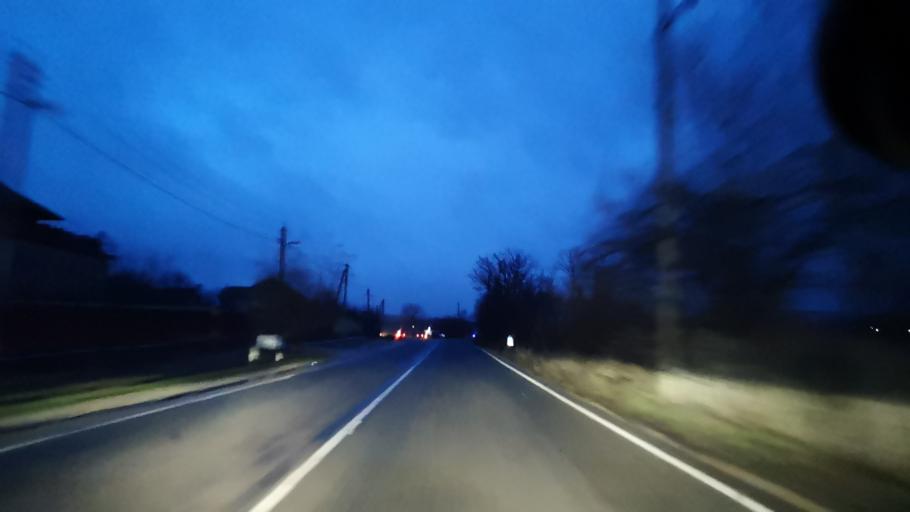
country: MD
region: Orhei
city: Orhei
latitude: 47.4537
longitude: 28.7919
